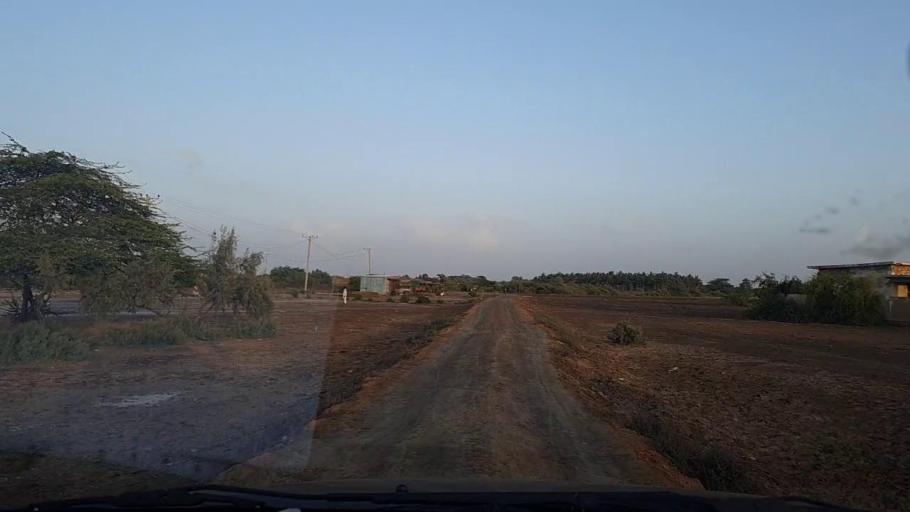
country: PK
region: Sindh
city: Keti Bandar
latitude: 24.1624
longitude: 67.6046
